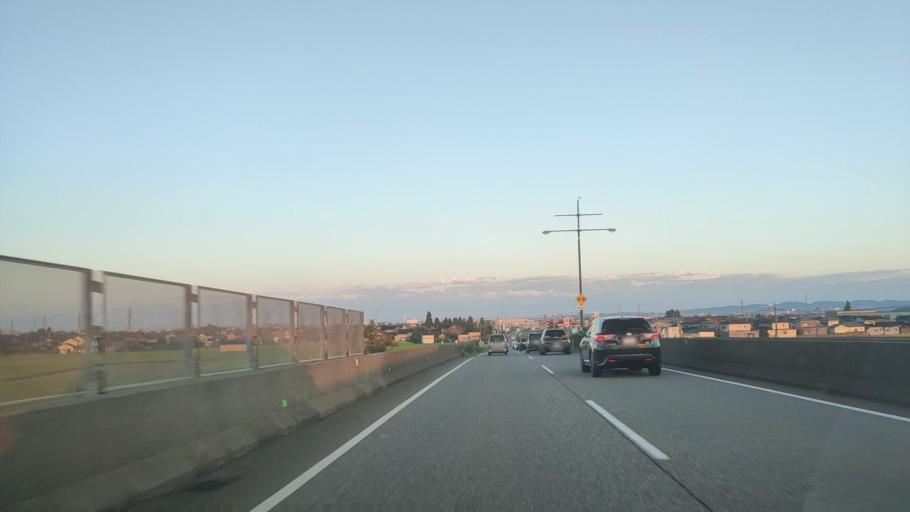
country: JP
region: Toyama
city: Nishishinminato
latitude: 36.7509
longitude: 137.0858
